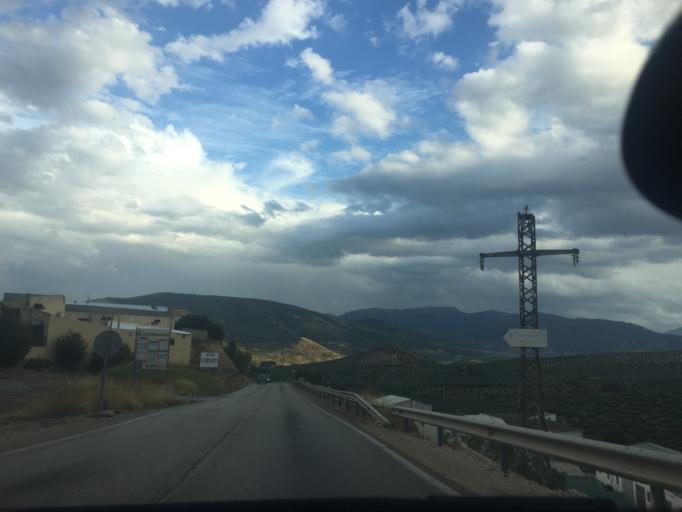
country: ES
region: Andalusia
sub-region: Provincia de Jaen
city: Jaen
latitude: 37.7660
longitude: -3.7739
